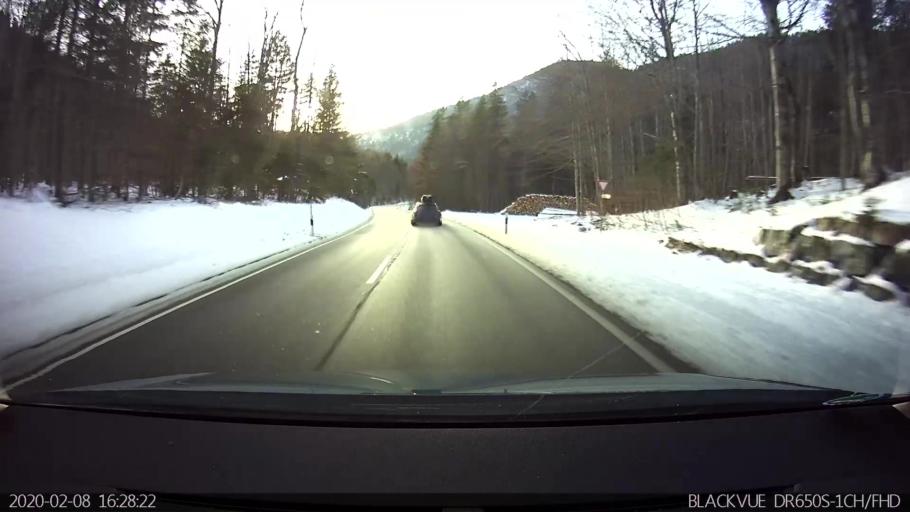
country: DE
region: Bavaria
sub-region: Upper Bavaria
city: Lenggries
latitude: 47.6015
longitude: 11.5727
